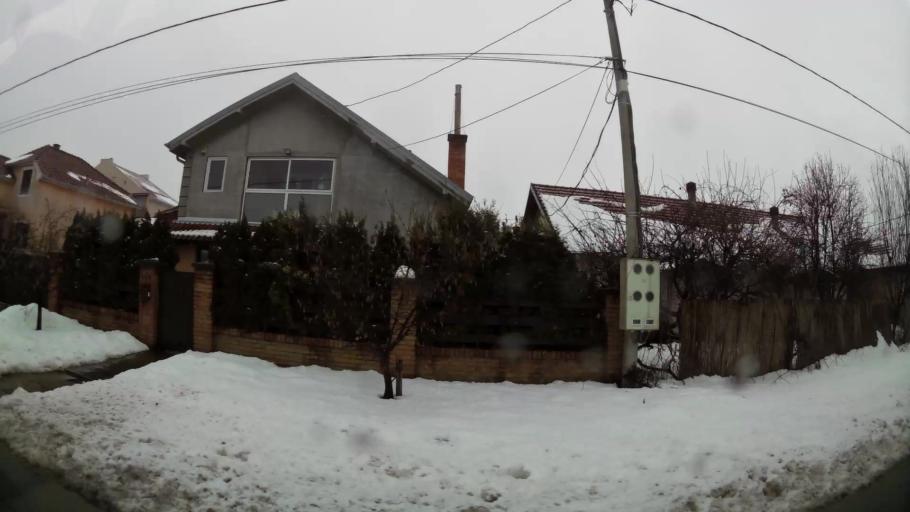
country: RS
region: Central Serbia
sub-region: Belgrade
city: Zemun
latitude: 44.8580
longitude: 20.3396
